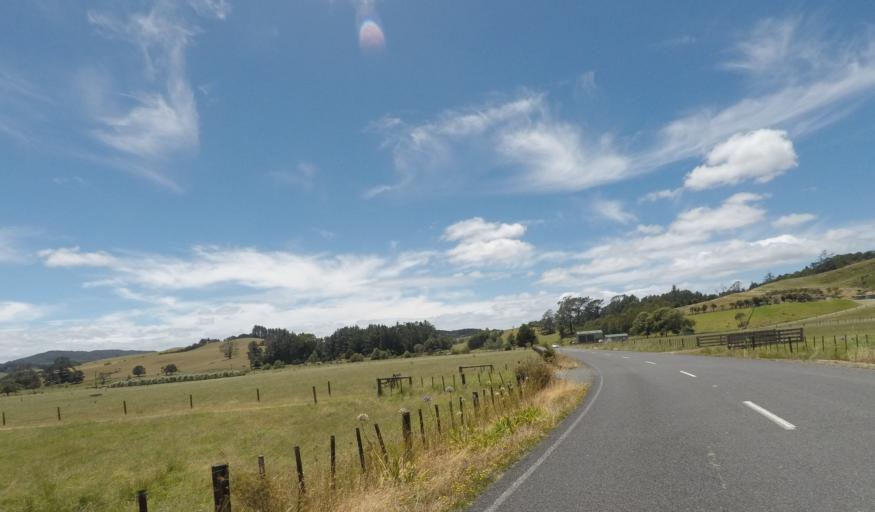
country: NZ
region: Northland
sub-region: Whangarei
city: Whangarei
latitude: -35.5486
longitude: 174.3015
